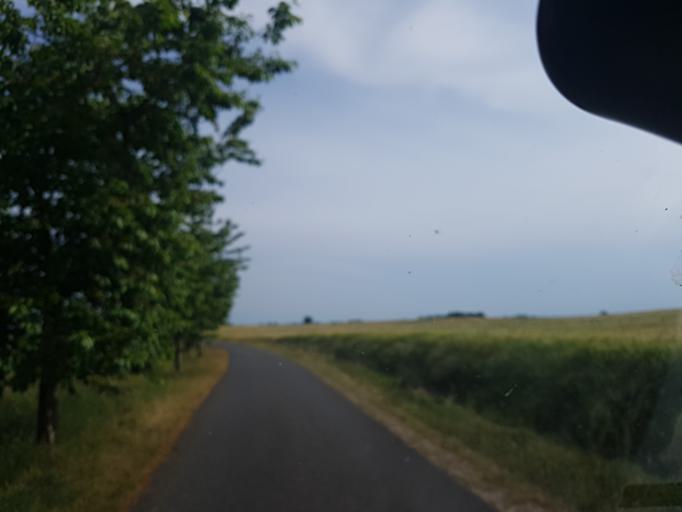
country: DE
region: Brandenburg
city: Niemegk
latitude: 51.9972
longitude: 12.6732
